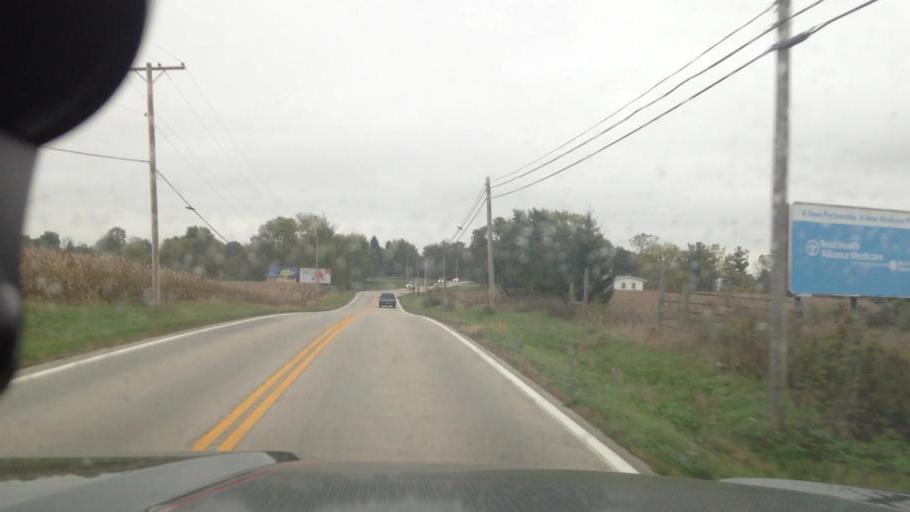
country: US
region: Ohio
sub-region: Darke County
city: Greenville
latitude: 40.1327
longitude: -84.6967
